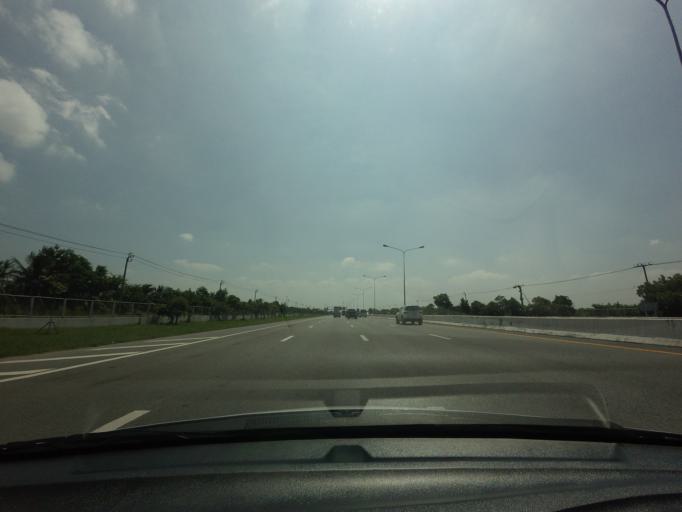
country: TH
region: Samut Prakan
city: Ban Khlong Bang Sao Thong
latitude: 13.6243
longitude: 100.9152
